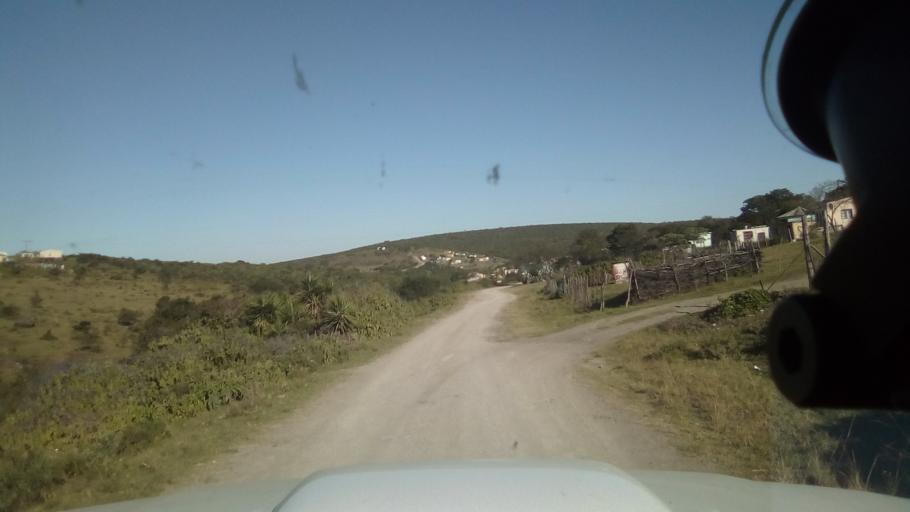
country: ZA
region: Eastern Cape
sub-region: Buffalo City Metropolitan Municipality
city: Bhisho
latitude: -32.7970
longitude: 27.3422
